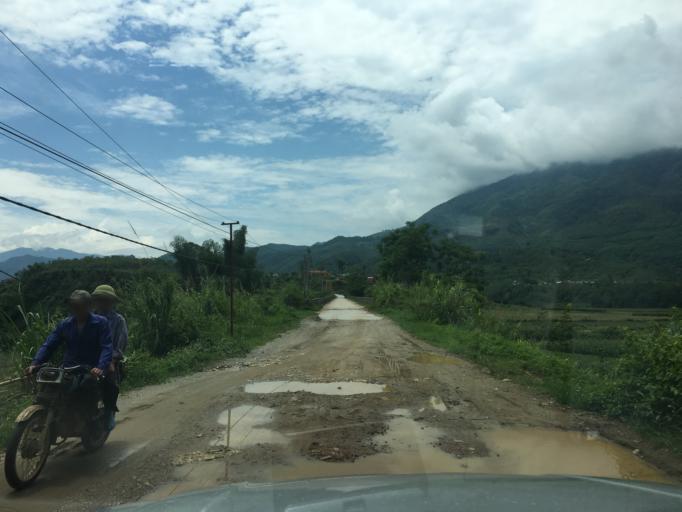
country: VN
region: Yen Bai
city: Son Thinh
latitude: 21.6552
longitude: 104.5069
